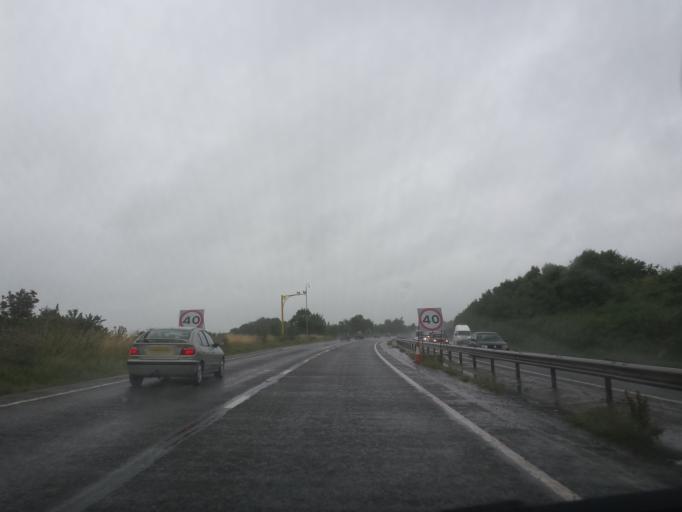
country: GB
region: England
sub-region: Warwickshire
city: Ryton on Dunsmore
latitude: 52.3843
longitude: -1.4484
